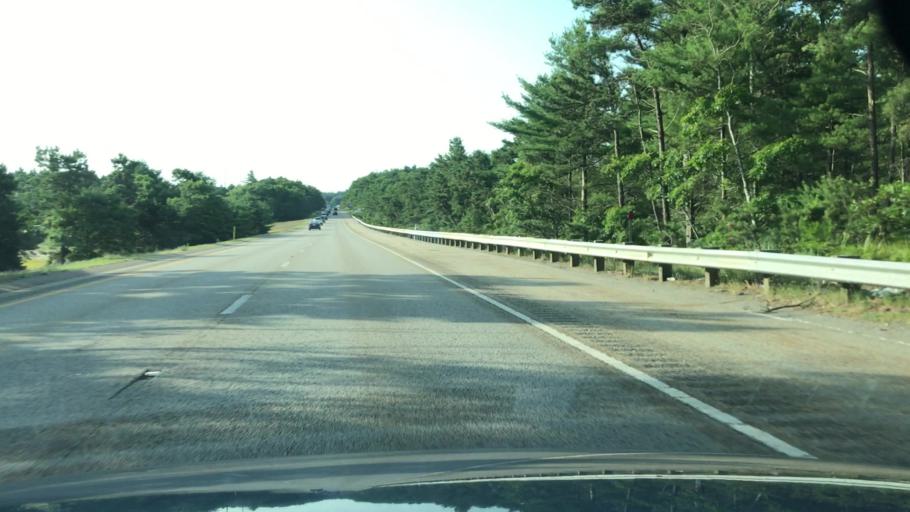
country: US
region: Massachusetts
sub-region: Plymouth County
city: White Island Shores
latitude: 41.8391
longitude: -70.5693
